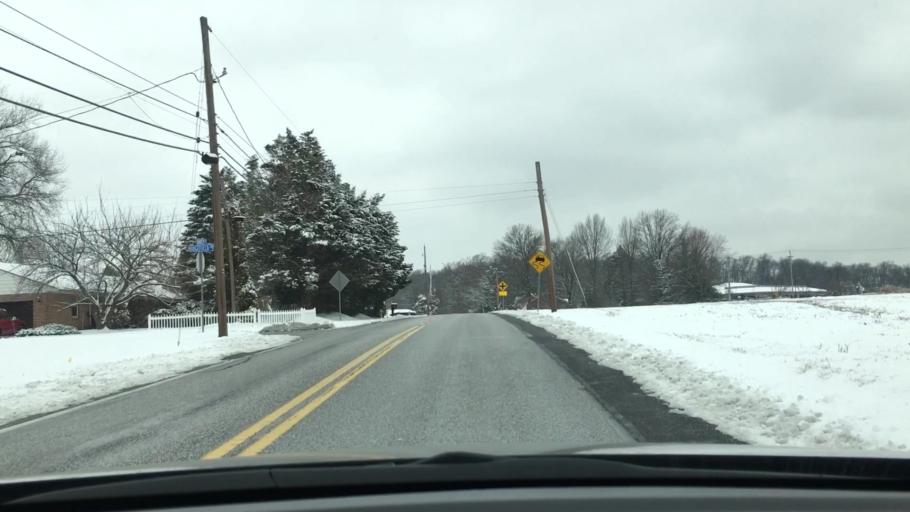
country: US
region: Pennsylvania
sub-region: York County
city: Grantley
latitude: 39.9210
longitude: -76.7162
